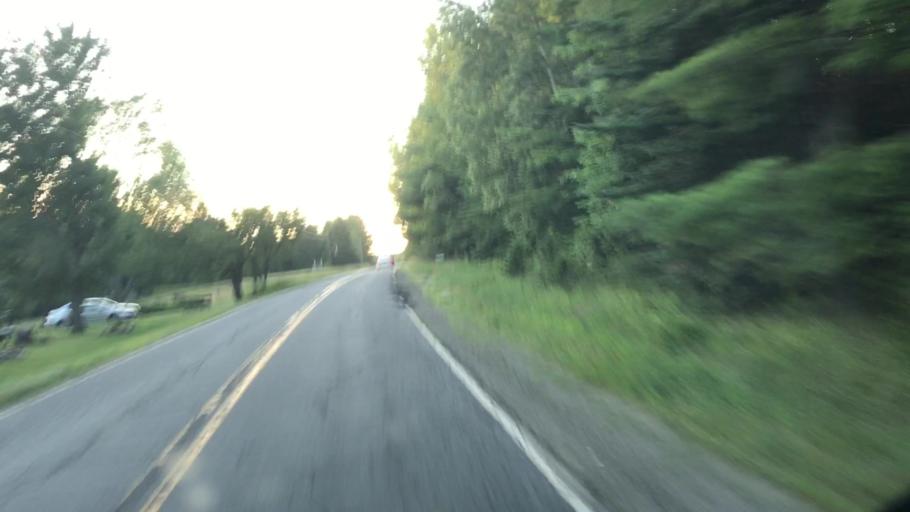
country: US
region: Maine
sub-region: Penobscot County
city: Medway
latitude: 45.5981
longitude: -68.2460
